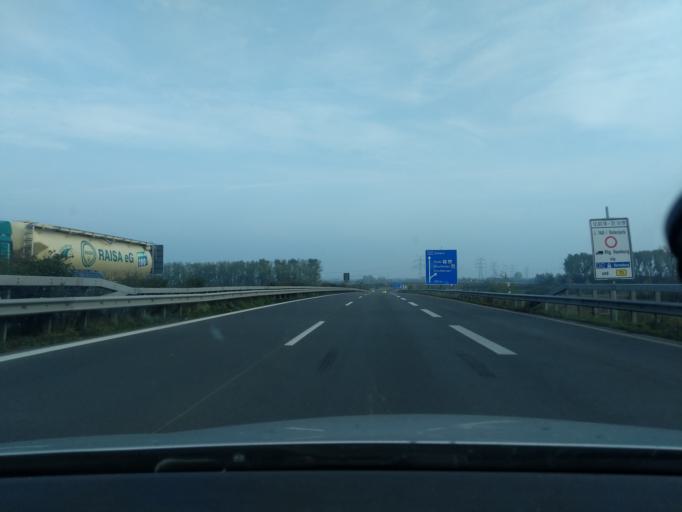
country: DE
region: Lower Saxony
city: Agathenburg
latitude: 53.5812
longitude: 9.5068
